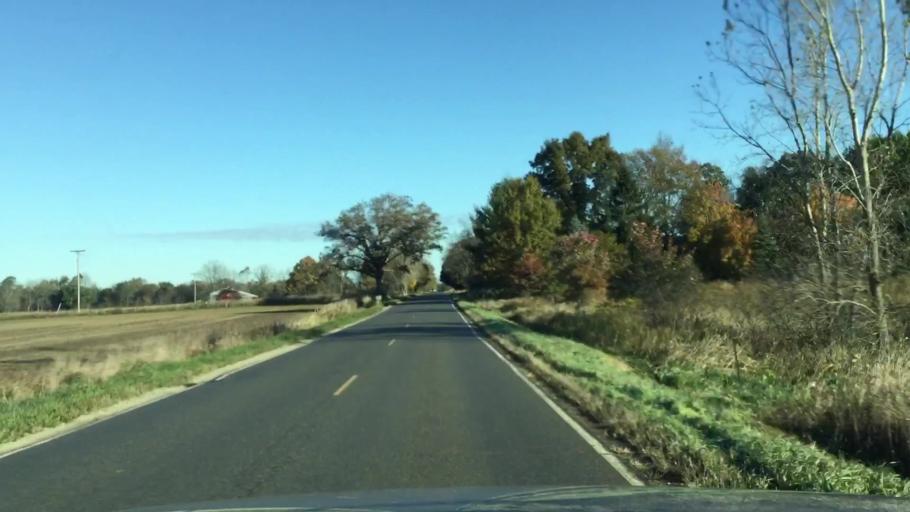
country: US
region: Michigan
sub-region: Genesee County
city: Argentine
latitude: 42.7863
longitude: -83.9425
